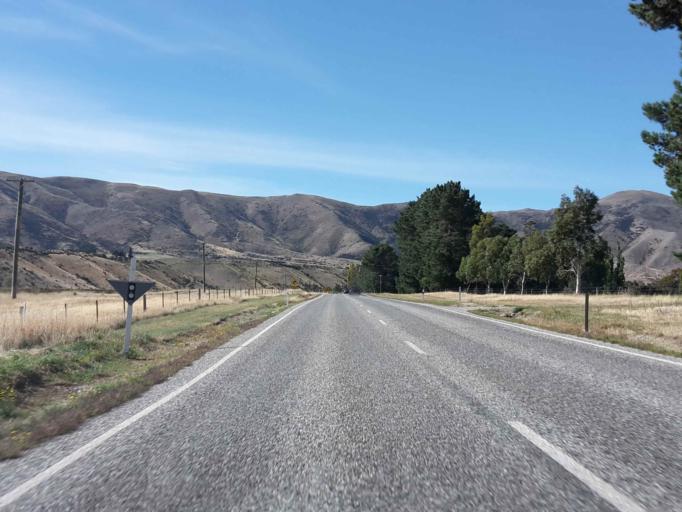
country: NZ
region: Otago
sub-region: Queenstown-Lakes District
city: Wanaka
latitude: -44.7333
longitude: 169.3100
